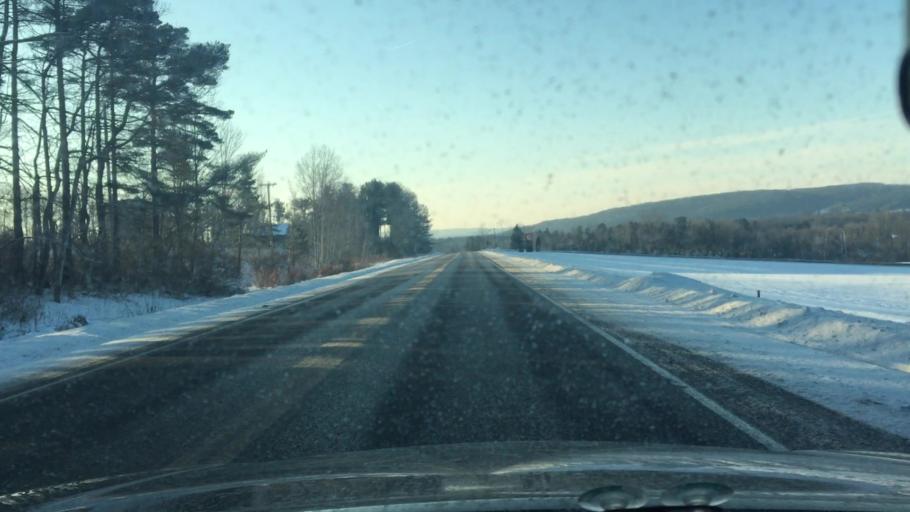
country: US
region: New York
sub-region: Chautauqua County
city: Lakewood
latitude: 42.0789
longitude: -79.3623
